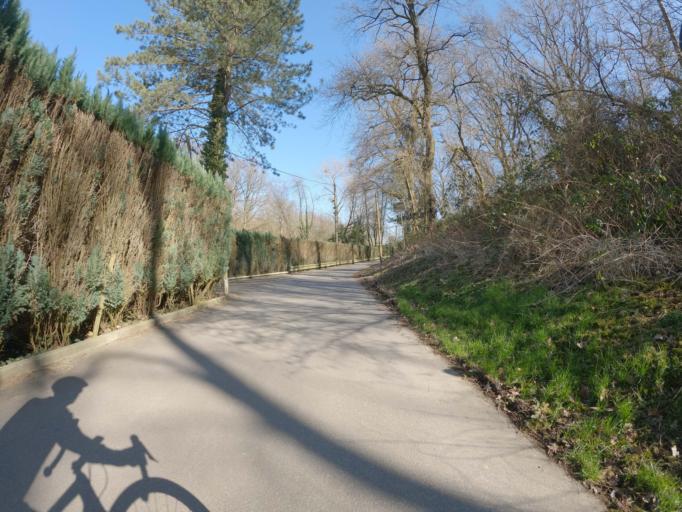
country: DE
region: North Rhine-Westphalia
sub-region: Regierungsbezirk Koln
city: Alsdorf
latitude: 50.8573
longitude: 6.1728
